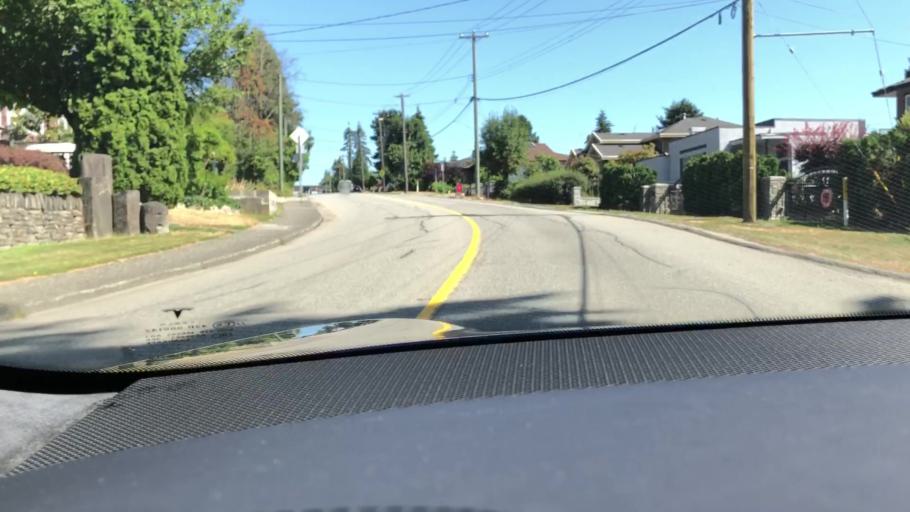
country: CA
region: British Columbia
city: Burnaby
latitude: 49.2113
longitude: -122.9719
